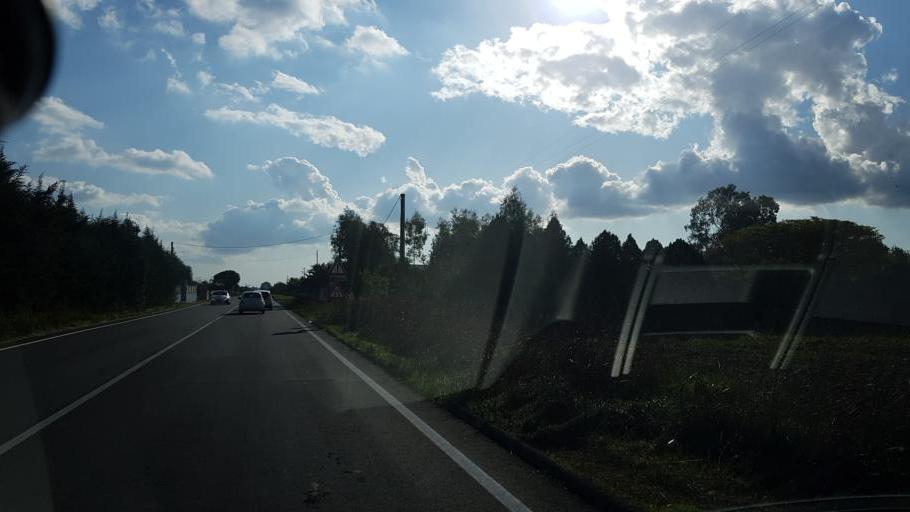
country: IT
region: Apulia
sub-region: Provincia di Lecce
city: Salice Salentino
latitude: 40.3692
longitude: 17.9670
